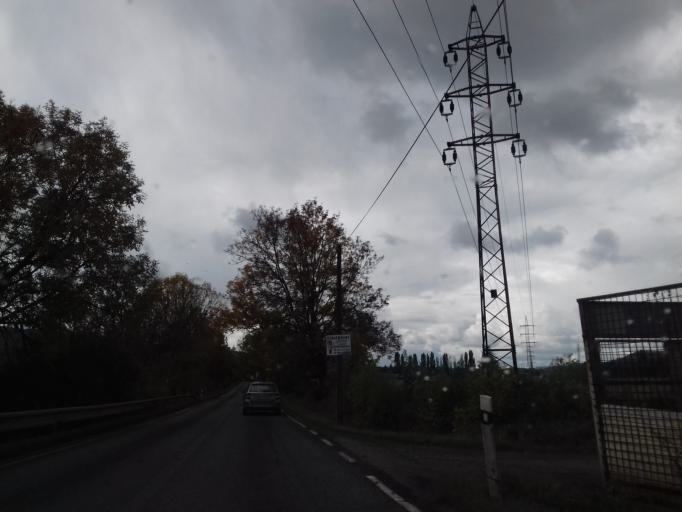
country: CZ
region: Central Bohemia
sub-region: Okres Praha-Zapad
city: Dobrichovice
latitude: 49.9390
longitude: 14.2876
